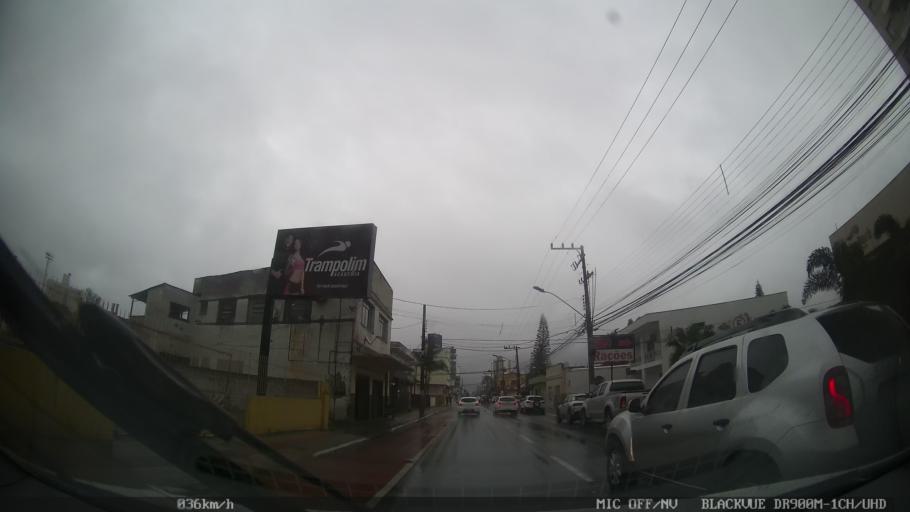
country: BR
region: Santa Catarina
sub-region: Itajai
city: Itajai
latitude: -26.9047
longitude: -48.6661
